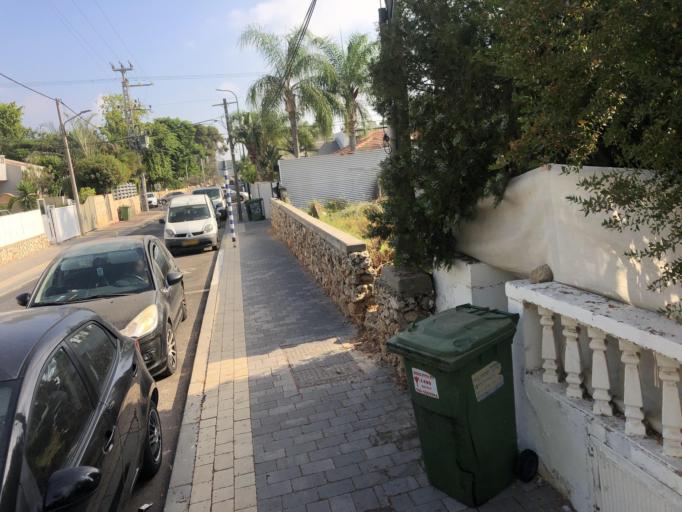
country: IL
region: Central District
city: Yehud
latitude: 32.0371
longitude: 34.8843
